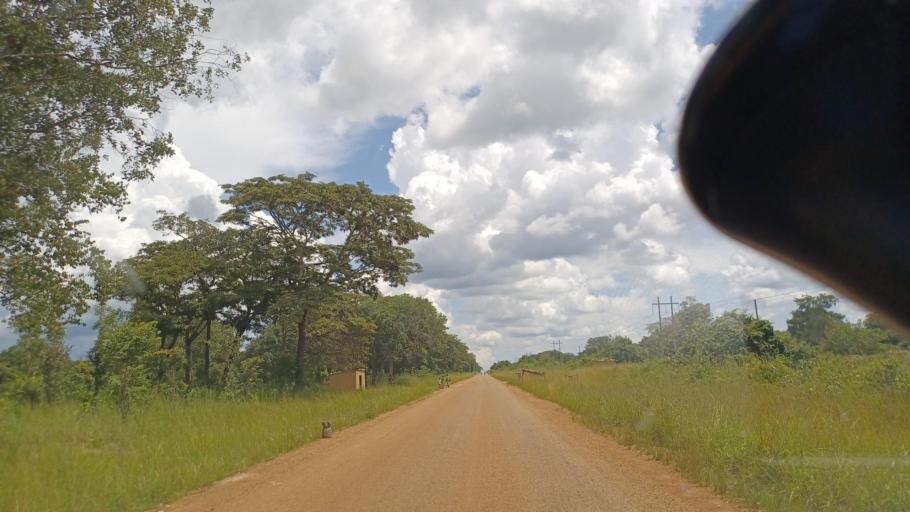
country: ZM
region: North-Western
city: Solwezi
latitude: -12.7001
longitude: 26.0363
